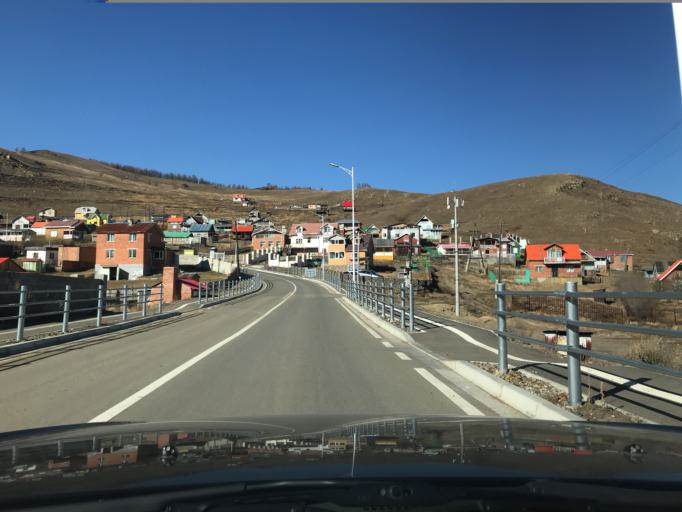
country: MN
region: Ulaanbaatar
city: Ulaanbaatar
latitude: 48.0379
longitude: 106.8984
